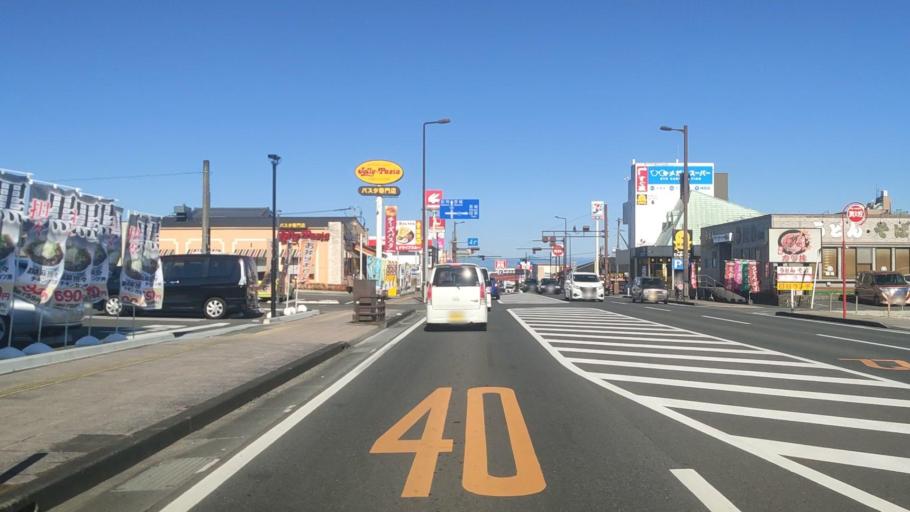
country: JP
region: Miyazaki
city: Miyakonojo
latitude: 31.7342
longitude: 131.0687
